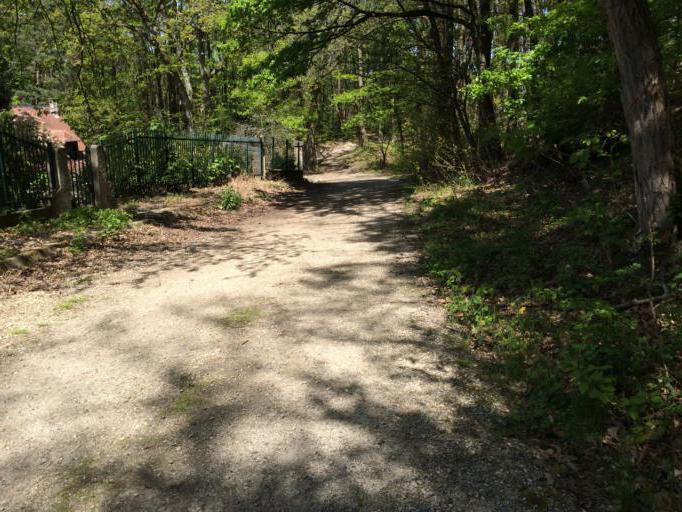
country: FR
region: Ile-de-France
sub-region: Departement de l'Essonne
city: Les Ulis
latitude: 48.6854
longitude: 2.1567
